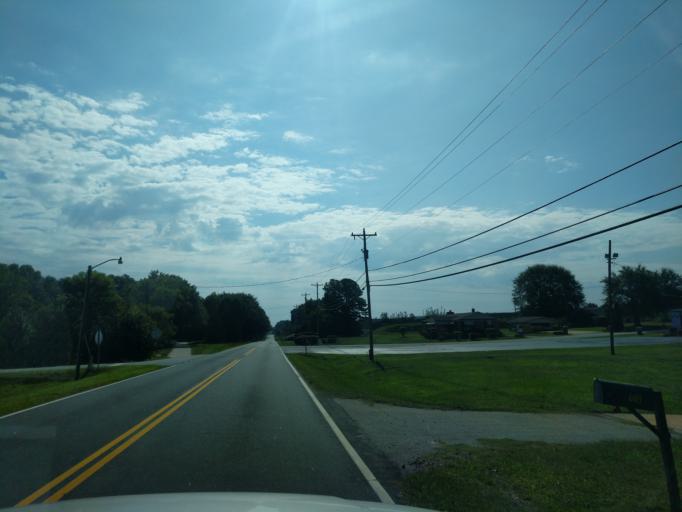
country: US
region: South Carolina
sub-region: Spartanburg County
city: Wellford
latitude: 34.9447
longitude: -82.1020
